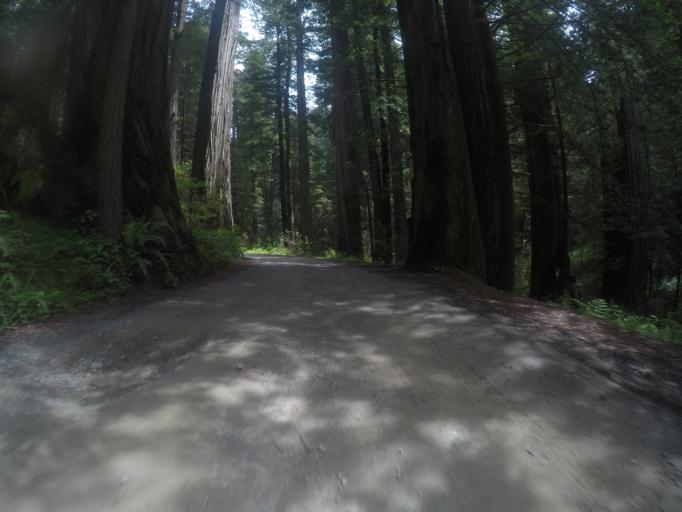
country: US
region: California
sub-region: Del Norte County
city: Bertsch-Oceanview
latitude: 41.7640
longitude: -124.1306
